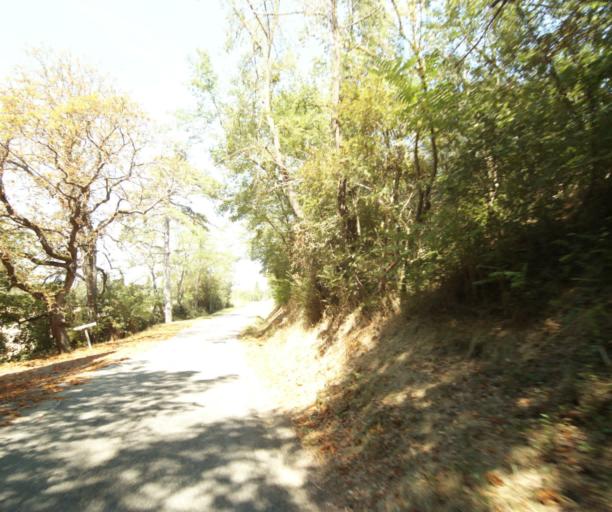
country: FR
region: Midi-Pyrenees
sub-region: Departement de l'Ariege
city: Lezat-sur-Leze
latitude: 43.3047
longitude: 1.3445
